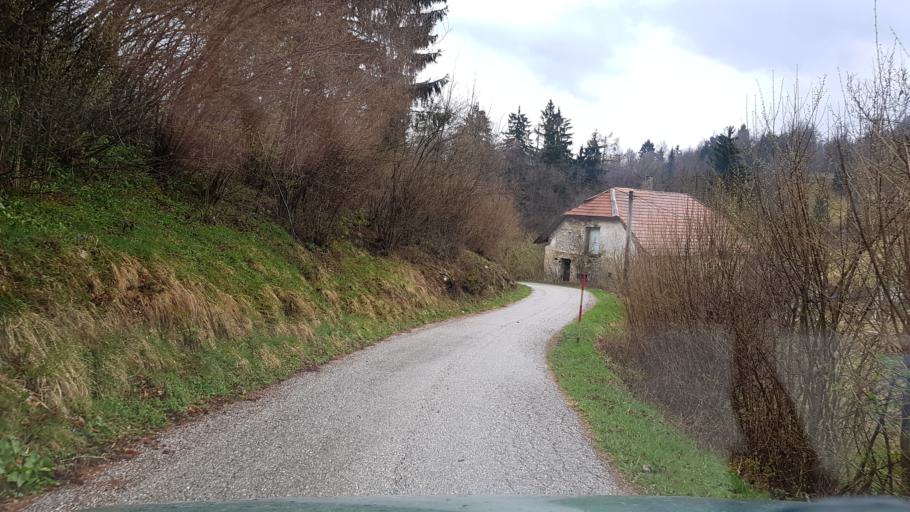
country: SI
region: Cerkno
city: Cerkno
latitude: 46.1432
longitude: 13.8816
